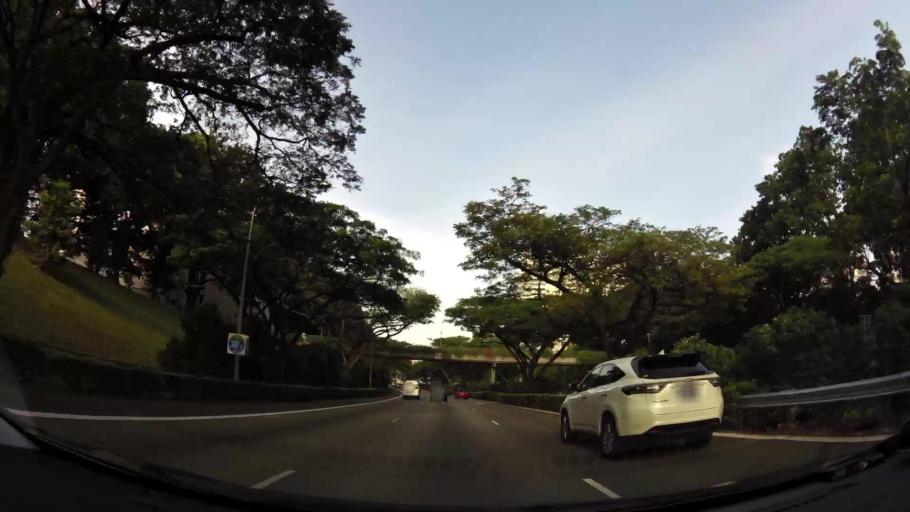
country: SG
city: Singapore
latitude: 1.3448
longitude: 103.7424
